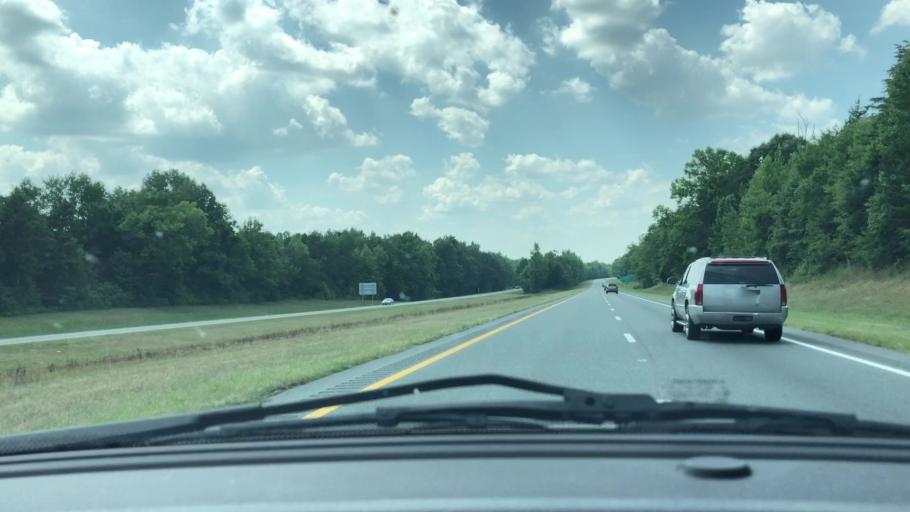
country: US
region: North Carolina
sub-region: Guilford County
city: Forest Oaks
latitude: 35.9730
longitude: -79.7222
